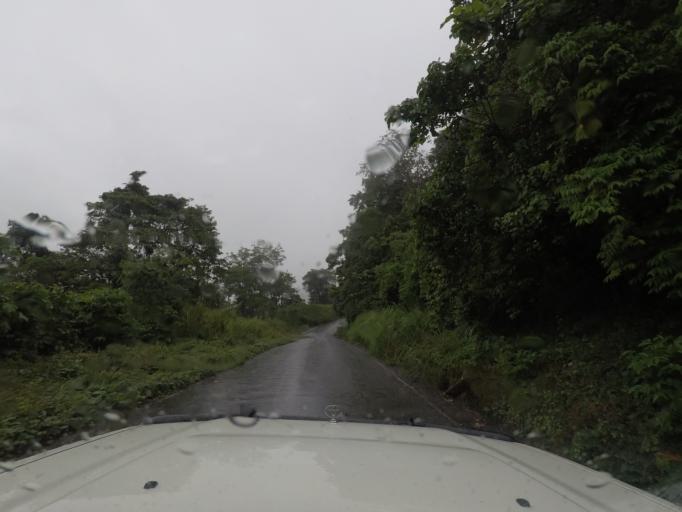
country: PG
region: Madang
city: Madang
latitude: -5.4350
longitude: 145.5481
